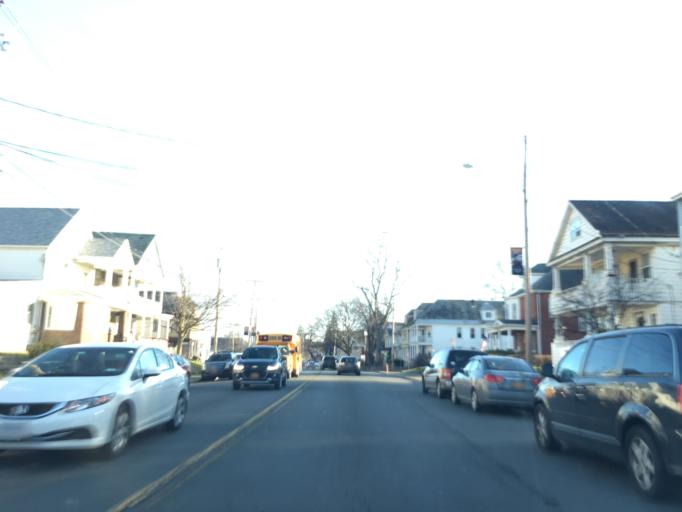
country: US
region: New York
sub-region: Rensselaer County
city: Wynantskill
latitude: 42.7070
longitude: -73.6617
